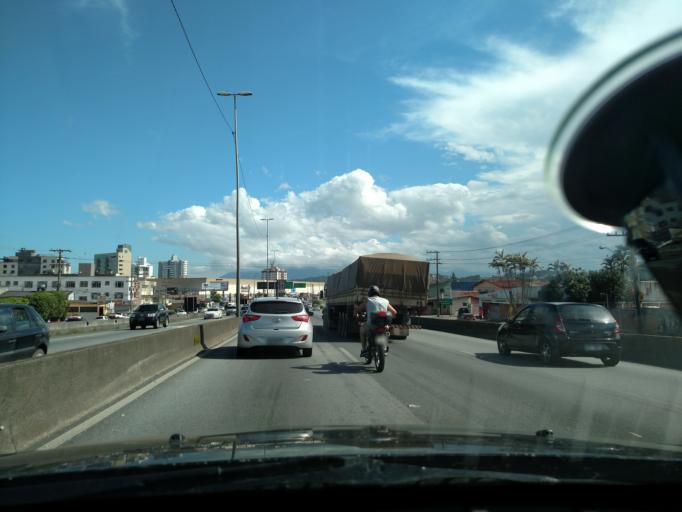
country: BR
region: Santa Catarina
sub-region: Sao Jose
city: Campinas
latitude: -27.5916
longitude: -48.6181
